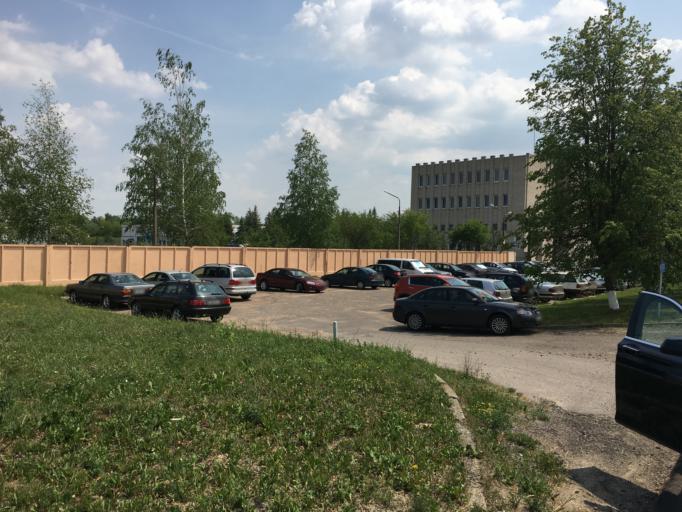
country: BY
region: Grodnenskaya
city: Hrodna
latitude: 53.7152
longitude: 23.8257
